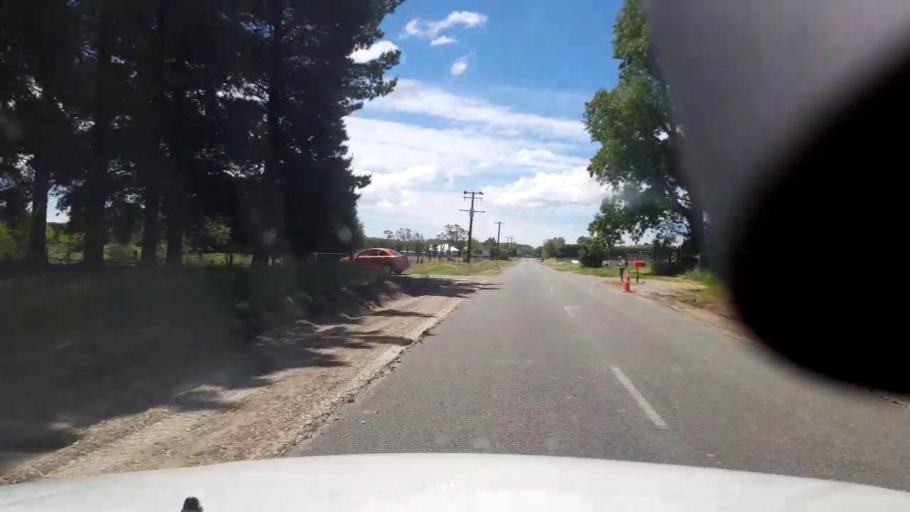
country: NZ
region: Canterbury
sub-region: Timaru District
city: Pleasant Point
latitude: -44.2753
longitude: 171.2521
